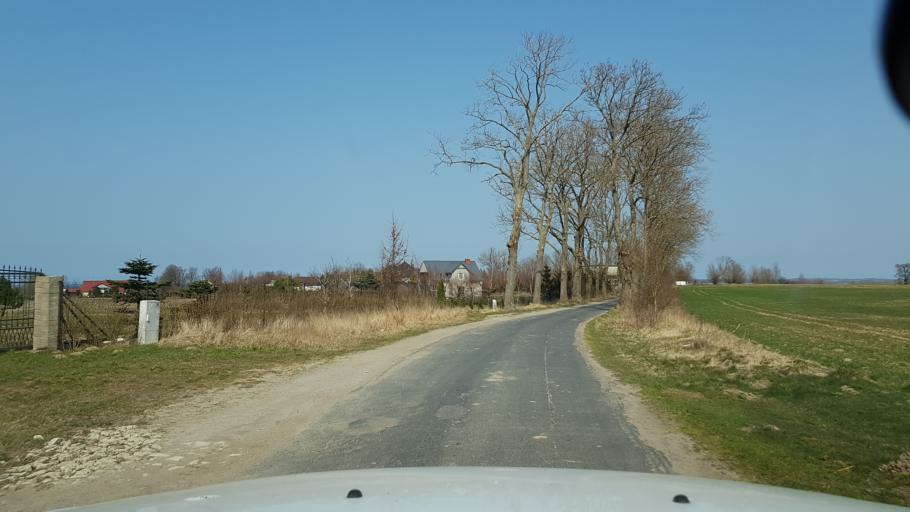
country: PL
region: West Pomeranian Voivodeship
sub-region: Powiat slawienski
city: Darlowo
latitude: 54.4538
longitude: 16.4336
